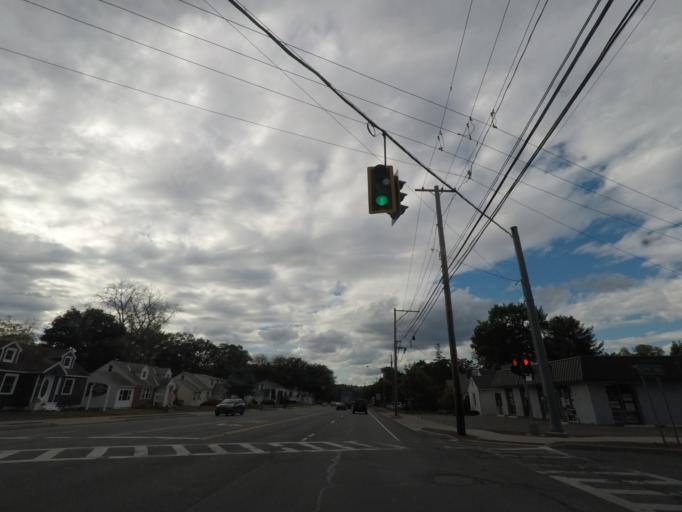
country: US
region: New York
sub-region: Albany County
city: Westmere
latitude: 42.6911
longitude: -73.8689
